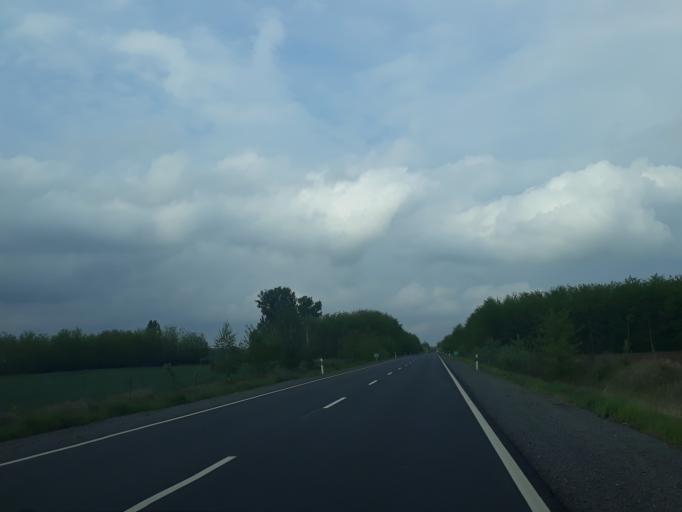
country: HU
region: Szabolcs-Szatmar-Bereg
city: Nyirtass
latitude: 48.1291
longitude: 22.0125
